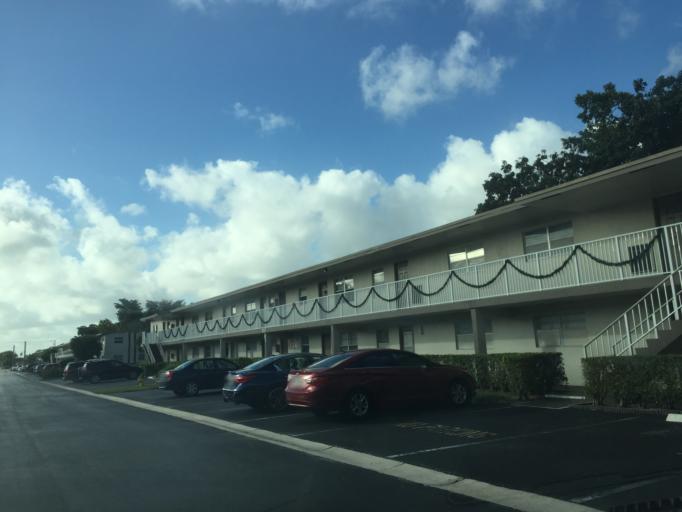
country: US
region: Florida
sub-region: Broward County
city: North Lauderdale
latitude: 26.2379
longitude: -80.2333
